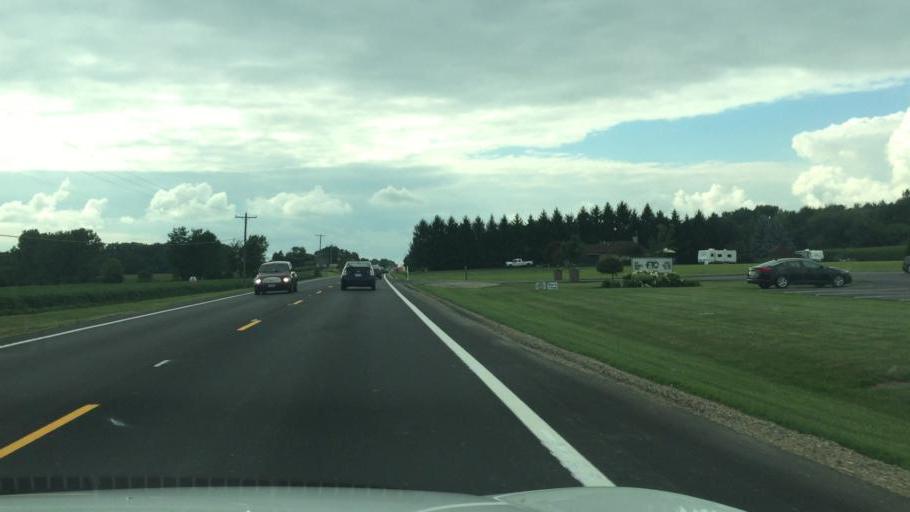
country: US
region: Ohio
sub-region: Champaign County
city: Urbana
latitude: 40.0935
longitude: -83.7002
